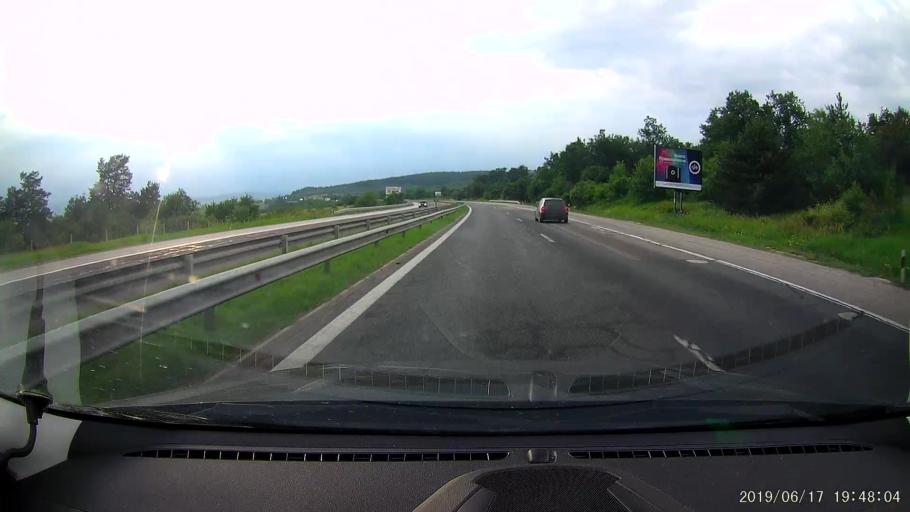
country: BG
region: Sofiya
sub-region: Obshtina Ikhtiman
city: Ikhtiman
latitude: 42.4620
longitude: 23.8323
